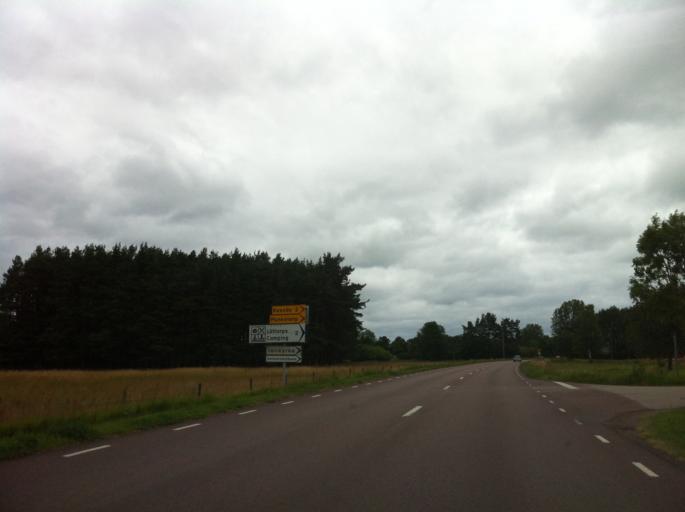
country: SE
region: Kalmar
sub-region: Borgholms Kommun
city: Borgholm
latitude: 57.1882
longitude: 17.0304
